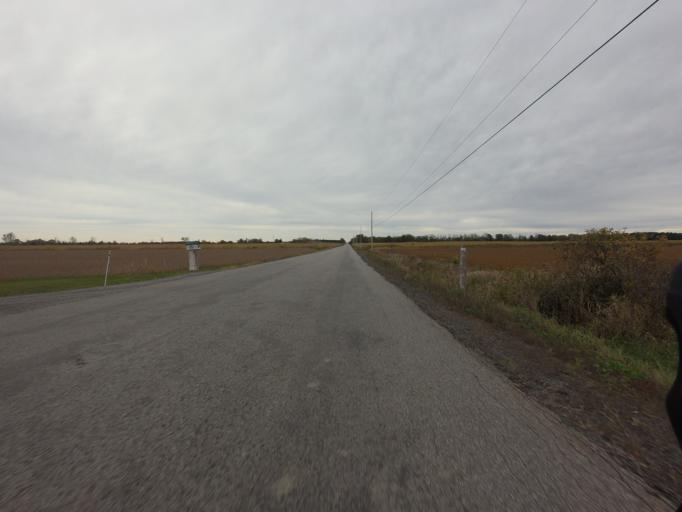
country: CA
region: Ontario
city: Bells Corners
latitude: 45.0976
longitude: -75.7472
